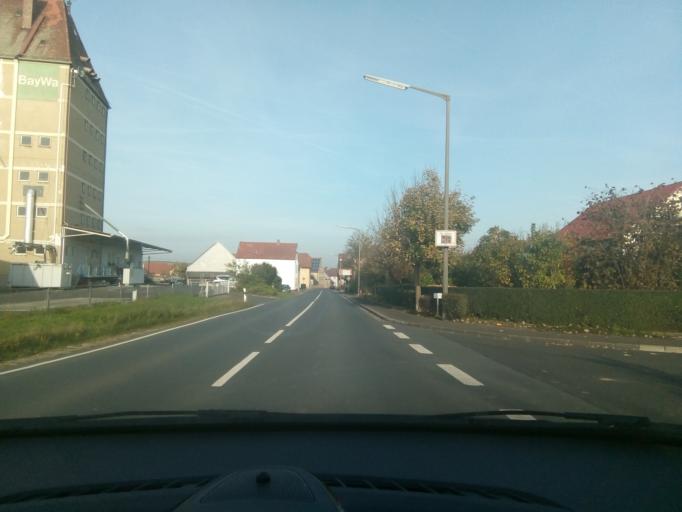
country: DE
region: Bavaria
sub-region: Regierungsbezirk Unterfranken
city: Prosselsheim
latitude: 49.8634
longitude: 10.1234
